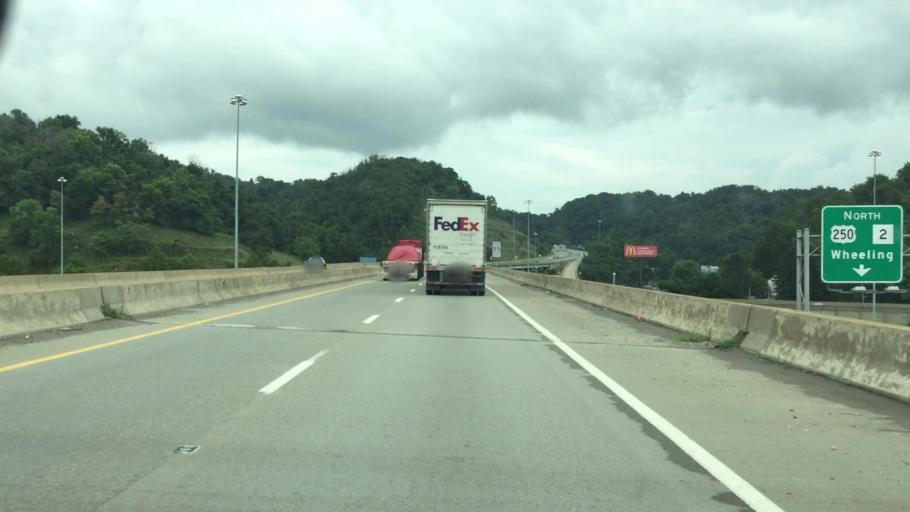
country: US
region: West Virginia
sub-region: Ohio County
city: Wheeling
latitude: 40.0509
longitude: -80.7238
